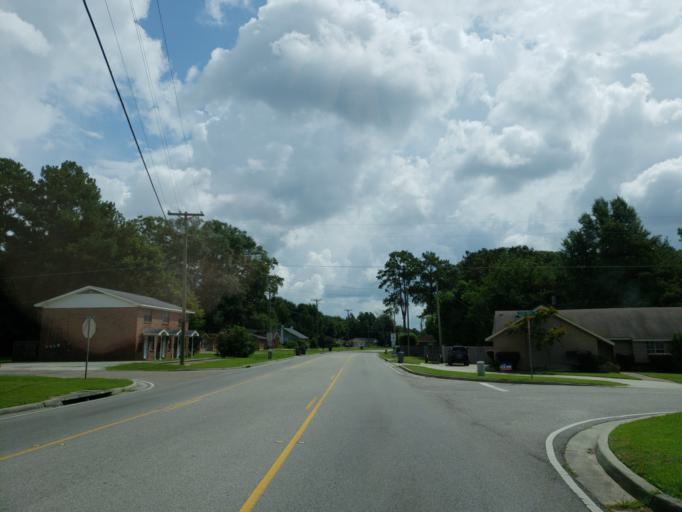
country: US
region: Mississippi
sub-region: Lamar County
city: Arnold Line
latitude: 31.3364
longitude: -89.3626
